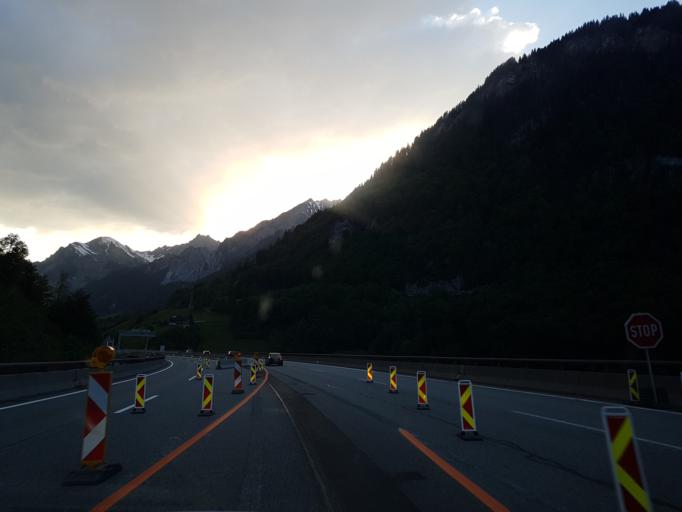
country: AT
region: Vorarlberg
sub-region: Politischer Bezirk Bludenz
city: Klosterle
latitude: 47.1301
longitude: 10.0827
